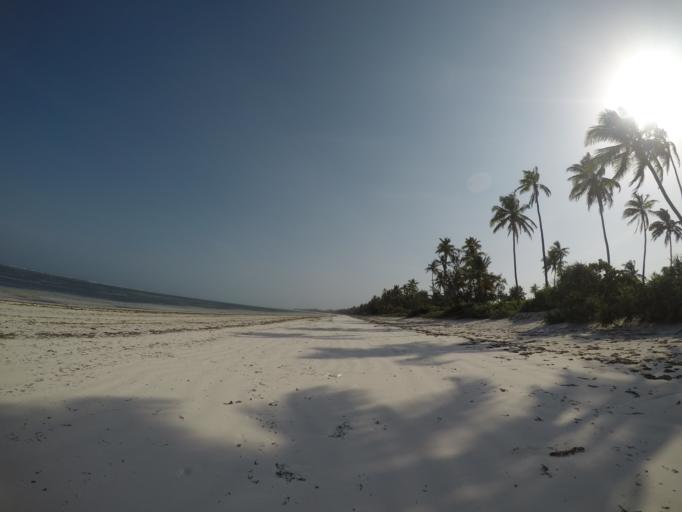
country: TZ
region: Zanzibar Central/South
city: Nganane
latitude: -6.2118
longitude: 39.5342
